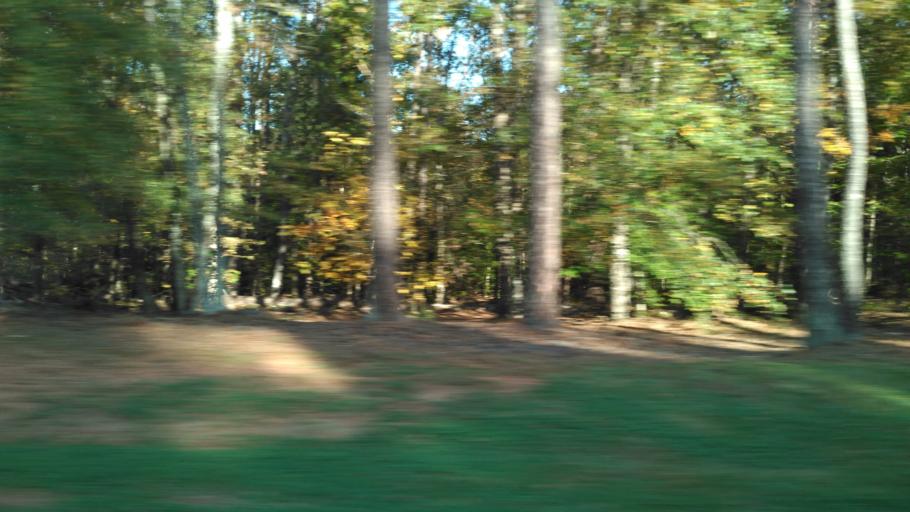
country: US
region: South Carolina
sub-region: Greenville County
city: Greer
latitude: 34.8830
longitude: -82.2155
